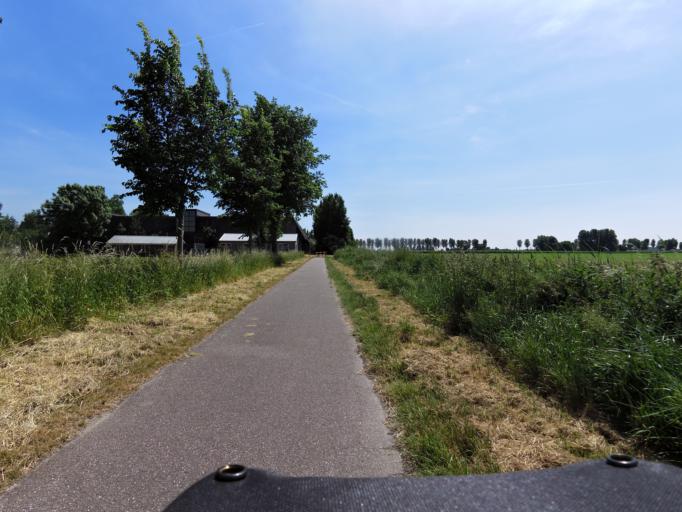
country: NL
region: South Holland
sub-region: Gemeente Spijkenisse
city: Spijkenisse
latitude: 51.7946
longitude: 4.3093
